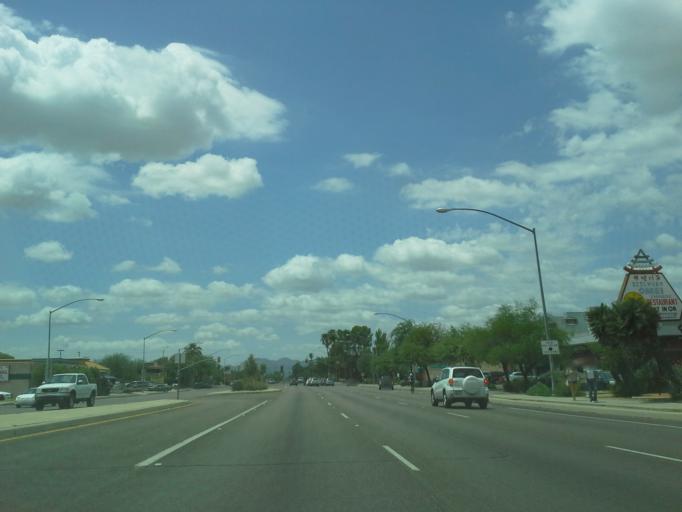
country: US
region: Arizona
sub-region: Pima County
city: Tucson
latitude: 32.2361
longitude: -110.9333
